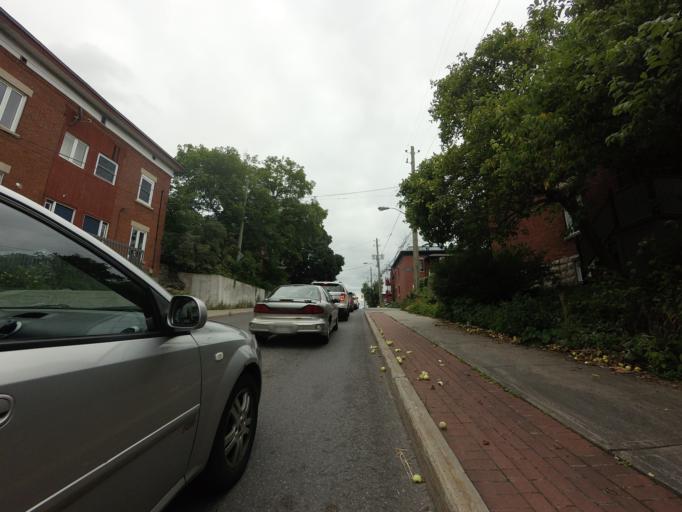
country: CA
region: Ontario
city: Ottawa
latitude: 45.4103
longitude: -75.7111
